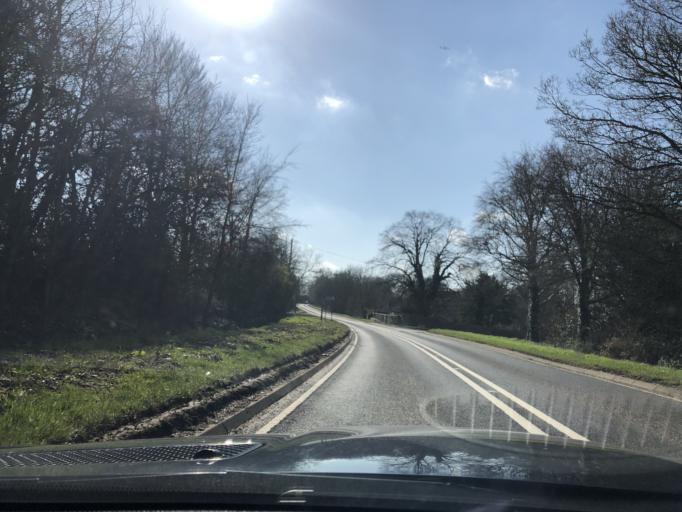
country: GB
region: England
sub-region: Warwickshire
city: Long Itchington
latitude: 52.3196
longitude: -1.4238
